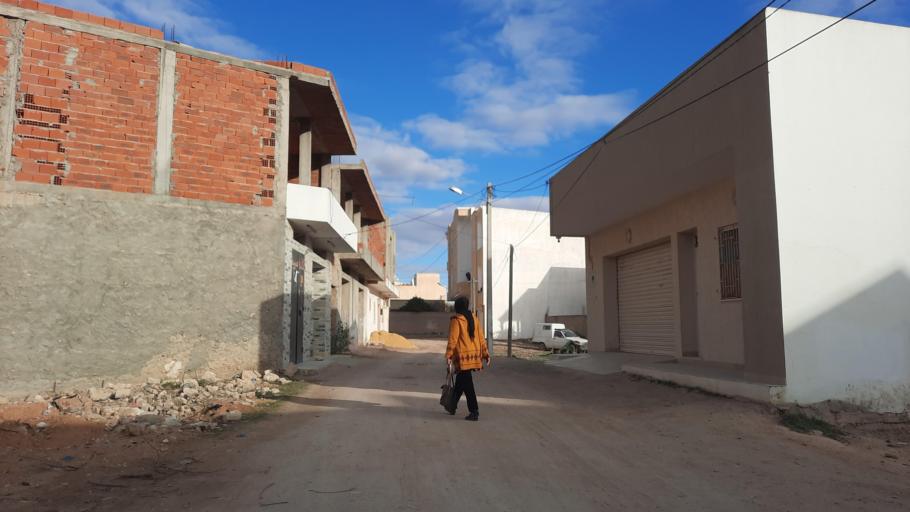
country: TN
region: Al Mahdiyah
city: El Jem
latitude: 35.2915
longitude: 10.7040
